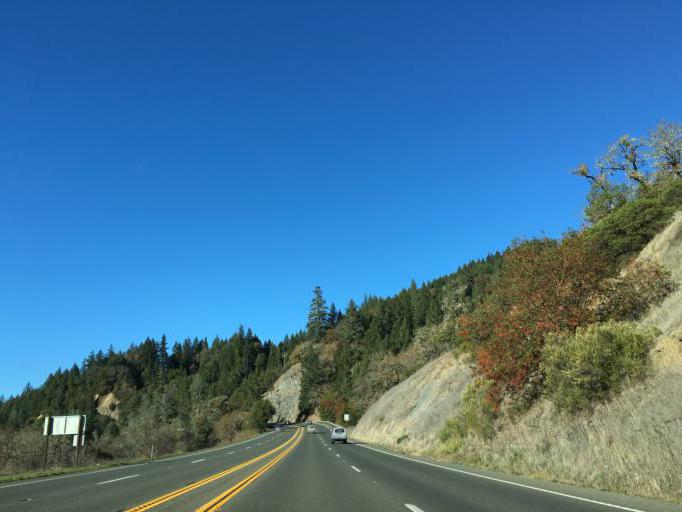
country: US
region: California
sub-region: Mendocino County
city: Brooktrails
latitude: 39.5196
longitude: -123.3921
